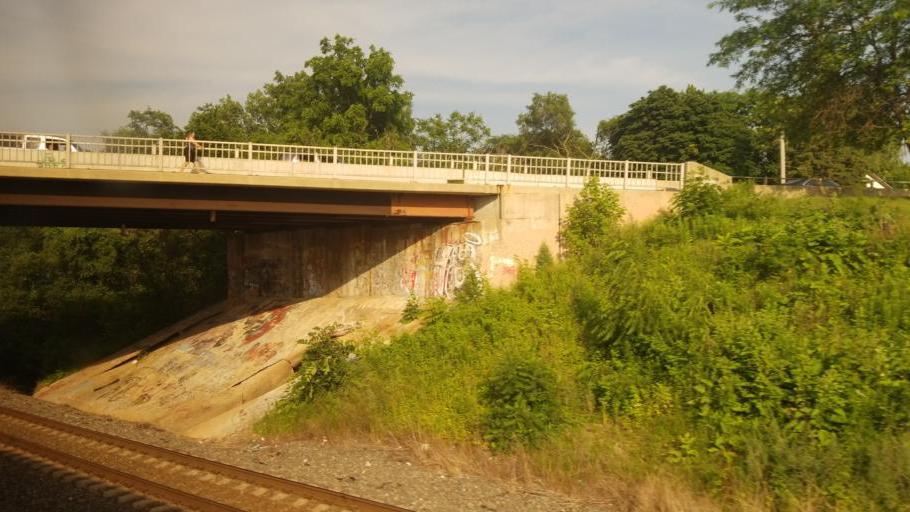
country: US
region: Illinois
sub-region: Kane County
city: Aurora
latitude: 41.7653
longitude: -88.3025
